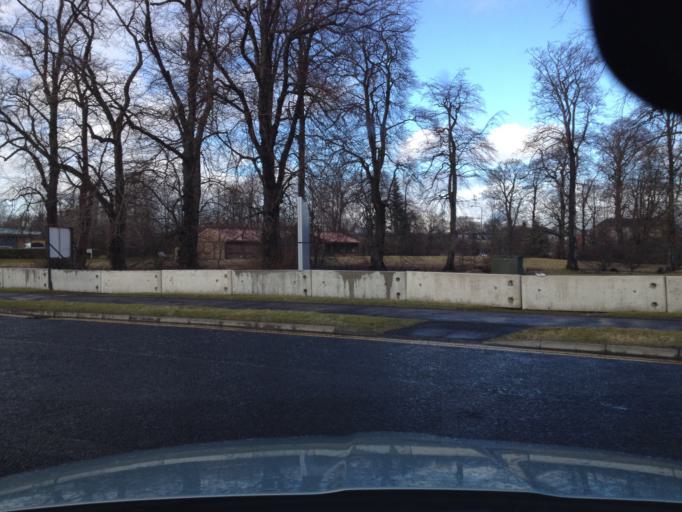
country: GB
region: Scotland
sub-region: West Lothian
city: Livingston
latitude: 55.8802
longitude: -3.5322
